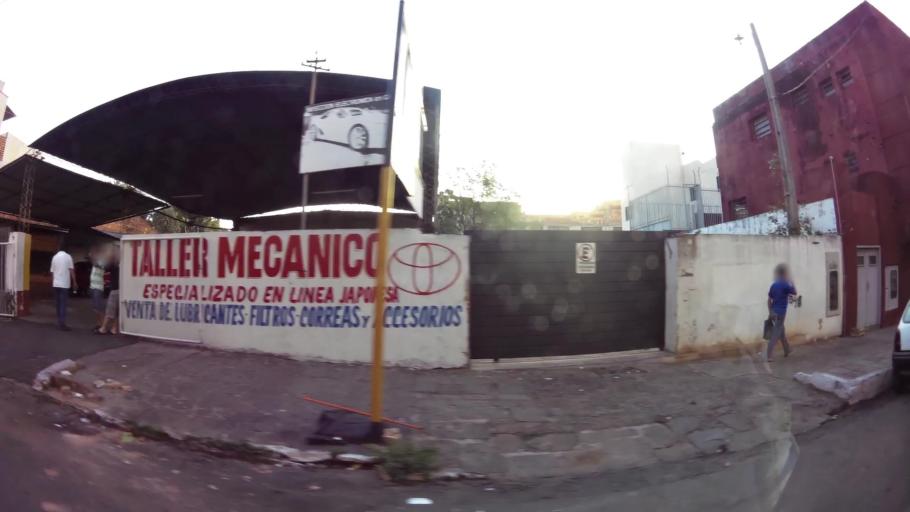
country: PY
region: Central
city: San Lorenzo
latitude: -25.3445
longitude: -57.5054
